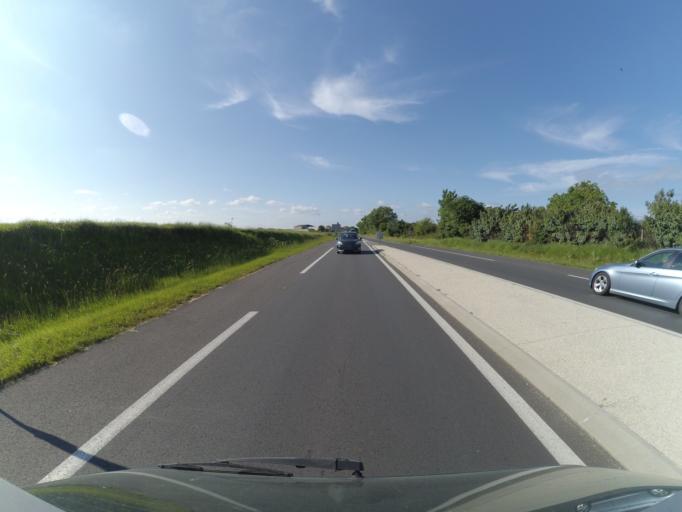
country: FR
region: Poitou-Charentes
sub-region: Departement de la Charente-Maritime
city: Saint-Sulpice-de-Royan
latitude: 45.6846
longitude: -0.9986
